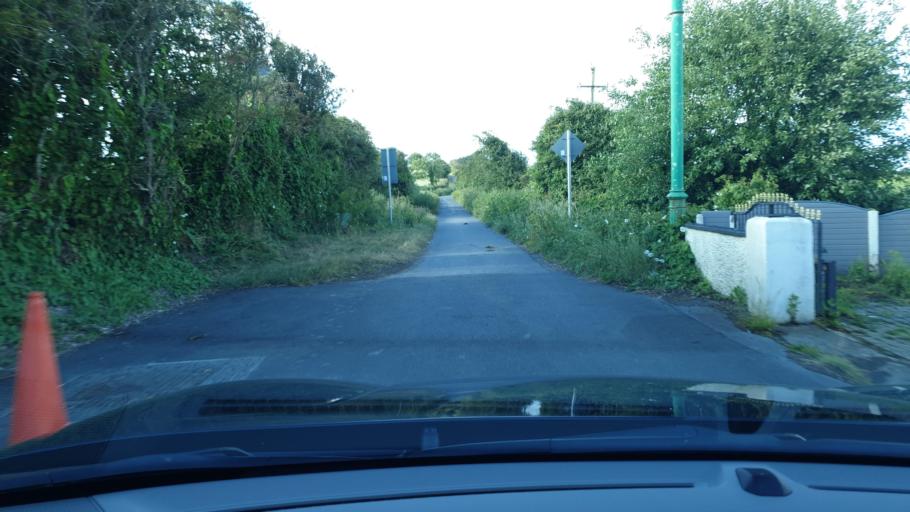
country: IE
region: Leinster
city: An Ros
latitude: 53.5477
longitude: -6.0859
